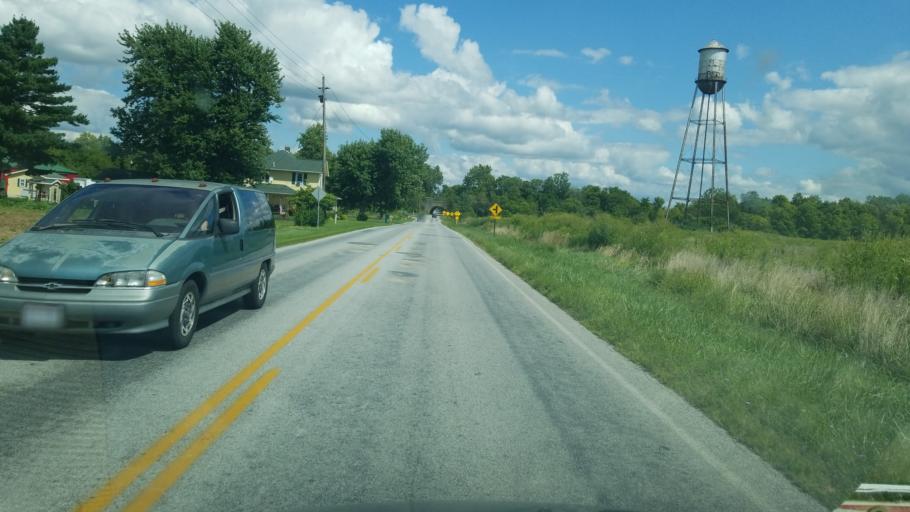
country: US
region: Ohio
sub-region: Allen County
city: Lima
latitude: 40.7884
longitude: -84.0969
